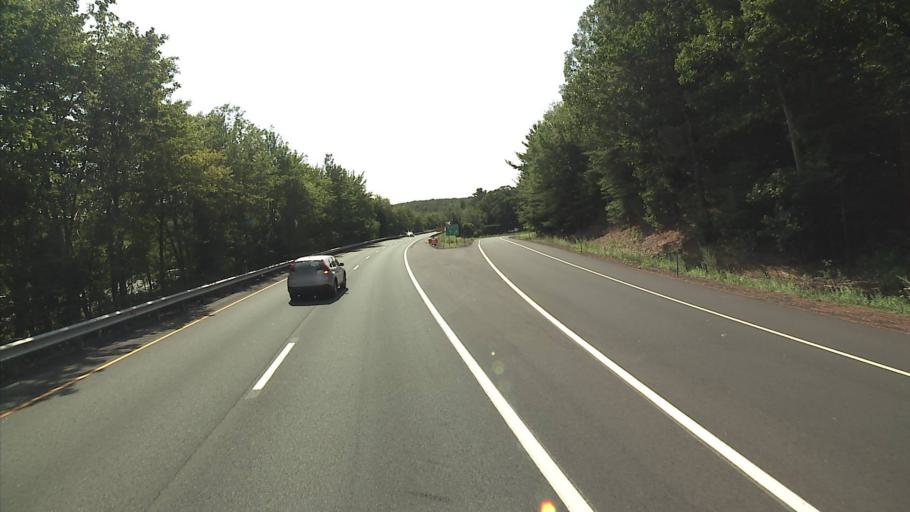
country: US
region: Connecticut
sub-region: Hartford County
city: Glastonbury Center
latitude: 41.7050
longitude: -72.5726
